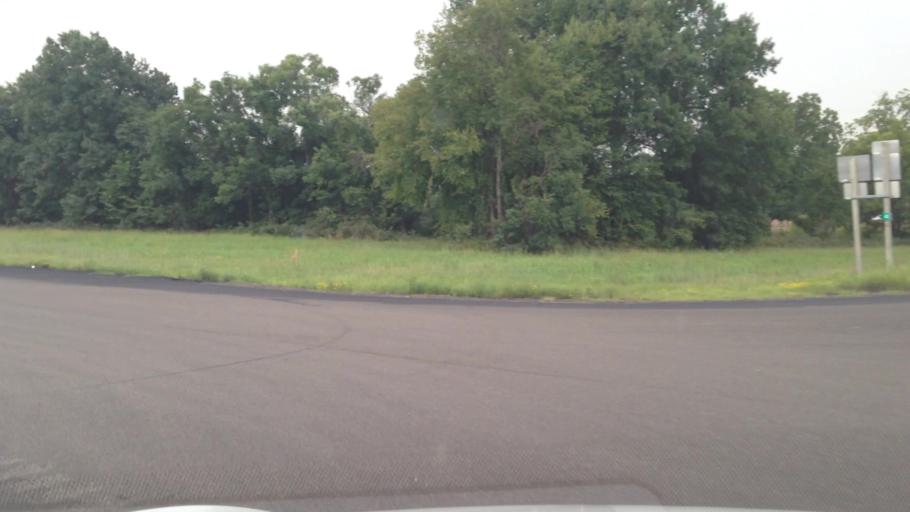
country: US
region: Kansas
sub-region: Cherokee County
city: Baxter Springs
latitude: 37.0553
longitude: -94.7352
